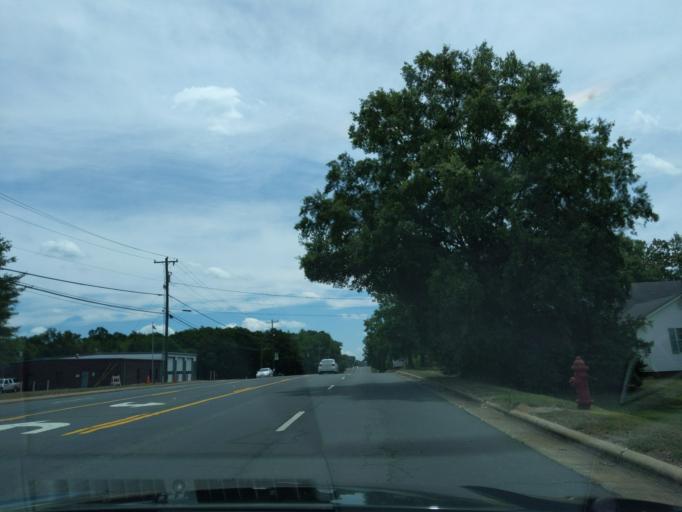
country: US
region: North Carolina
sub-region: Stanly County
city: Albemarle
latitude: 35.4706
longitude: -80.2658
